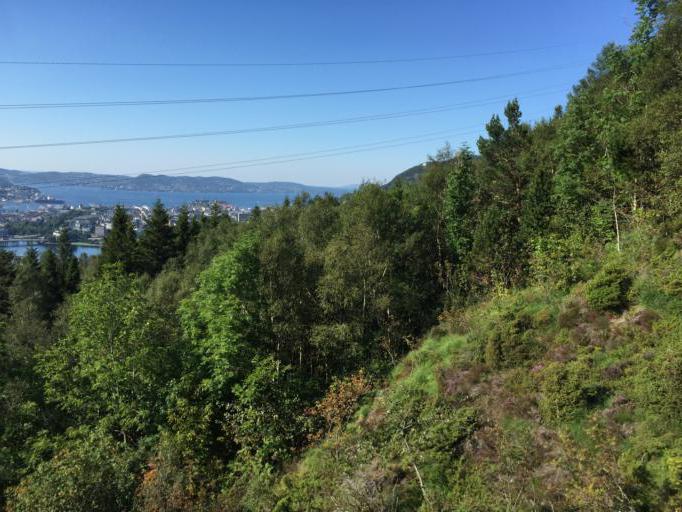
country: NO
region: Hordaland
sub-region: Bergen
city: Bergen
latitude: 60.3748
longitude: 5.3681
